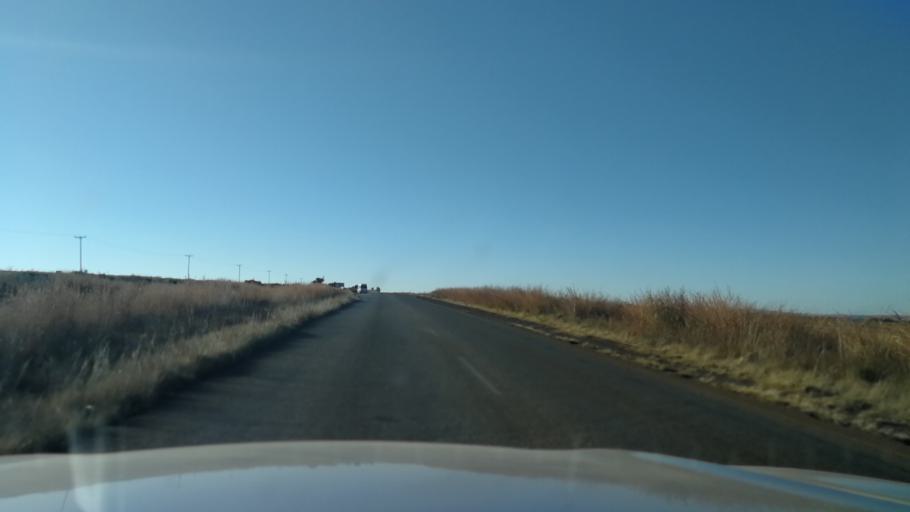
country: ZA
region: North-West
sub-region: Bojanala Platinum District Municipality
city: Rustenburg
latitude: -25.9644
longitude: 27.2141
